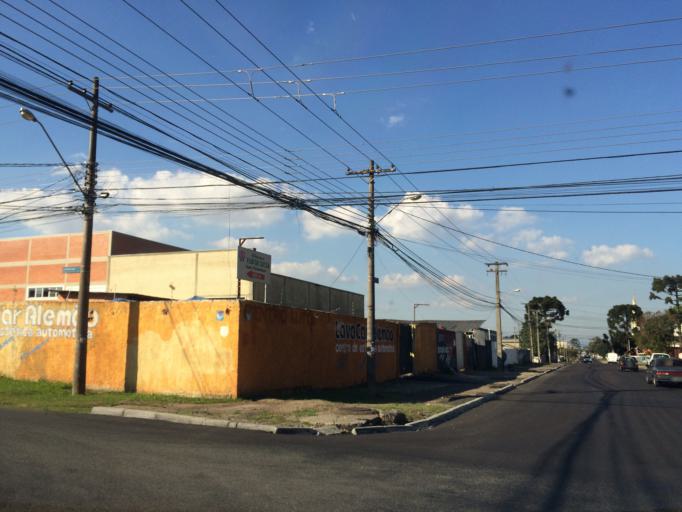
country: BR
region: Parana
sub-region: Sao Jose Dos Pinhais
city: Sao Jose dos Pinhais
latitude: -25.5100
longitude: -49.2322
